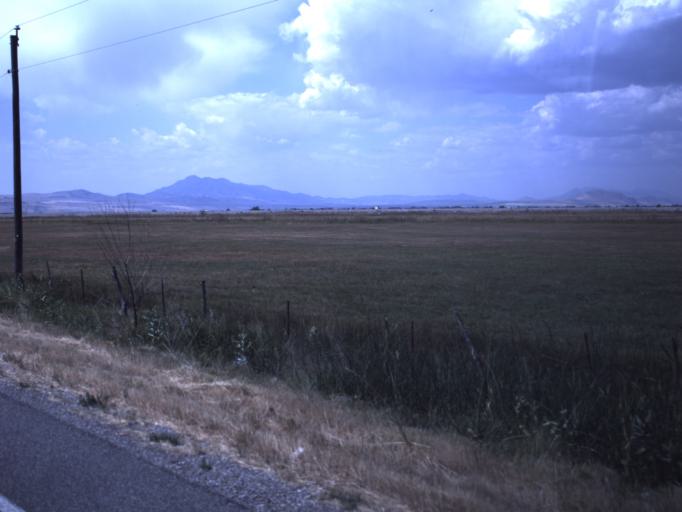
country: US
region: Utah
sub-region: Cache County
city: Logan
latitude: 41.7366
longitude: -111.8907
